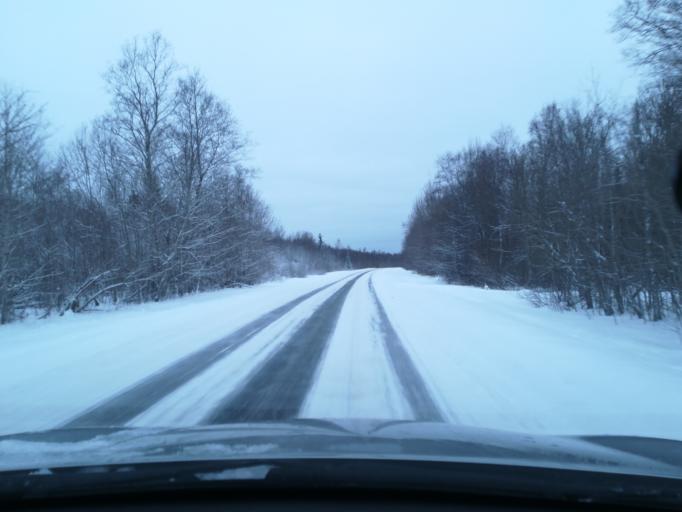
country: EE
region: Harju
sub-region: Keila linn
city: Keila
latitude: 59.3786
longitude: 24.3046
